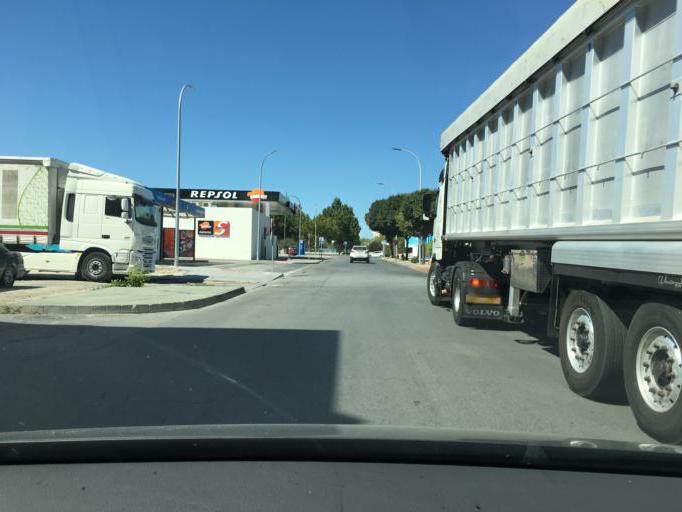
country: ES
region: Andalusia
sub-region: Provincia de Granada
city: Albolote
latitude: 37.2325
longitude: -3.6486
